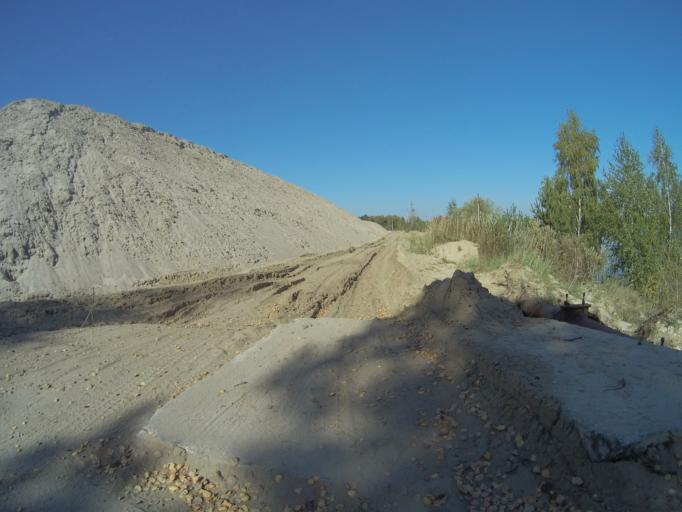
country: RU
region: Vladimir
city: Raduzhnyy
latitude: 56.0289
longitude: 40.3268
